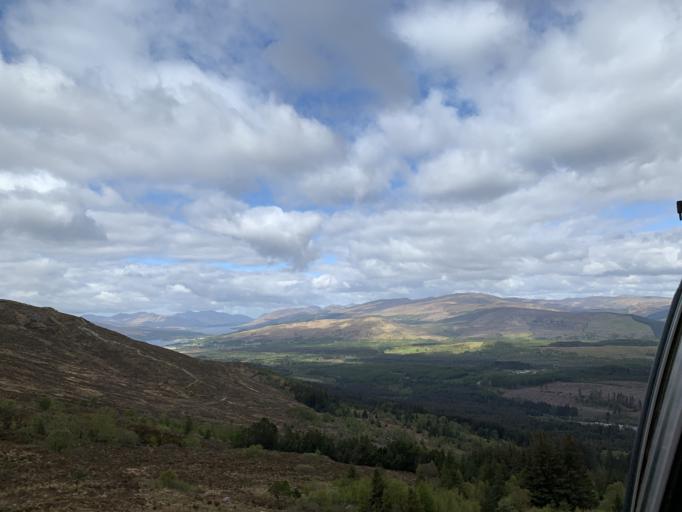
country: GB
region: Scotland
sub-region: Highland
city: Spean Bridge
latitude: 56.8429
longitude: -4.9832
